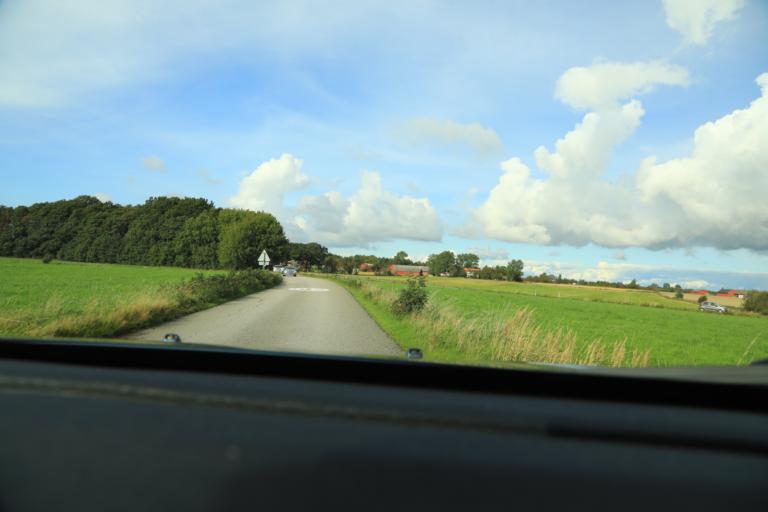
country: SE
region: Halland
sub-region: Varbergs Kommun
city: Traslovslage
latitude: 57.0442
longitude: 12.3162
